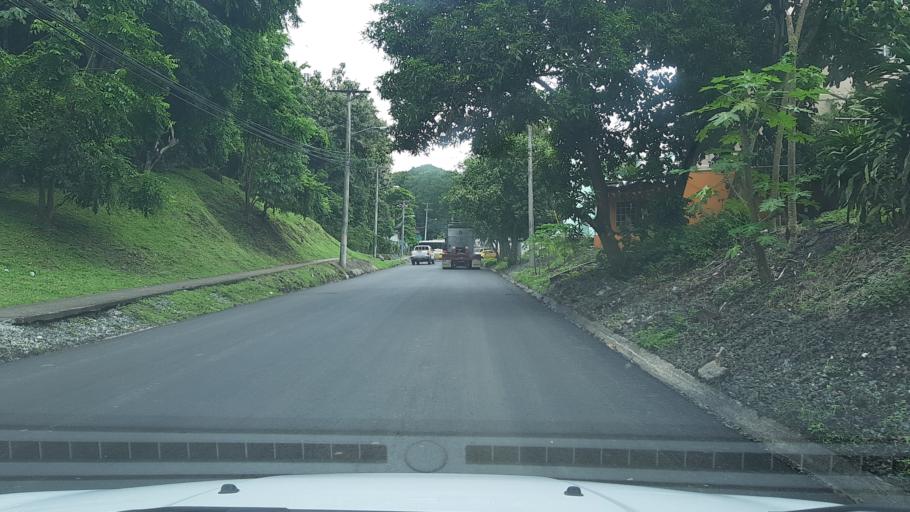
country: PA
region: Panama
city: San Miguelito
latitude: 9.0281
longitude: -79.4831
